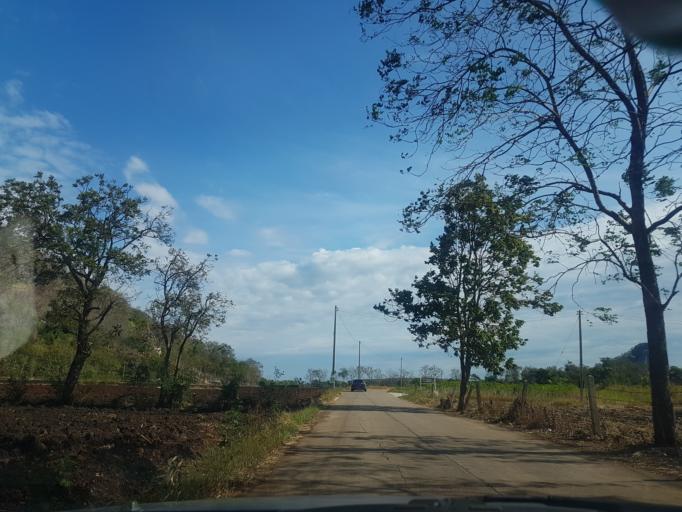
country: TH
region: Sara Buri
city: Phra Phutthabat
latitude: 14.8243
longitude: 100.7581
